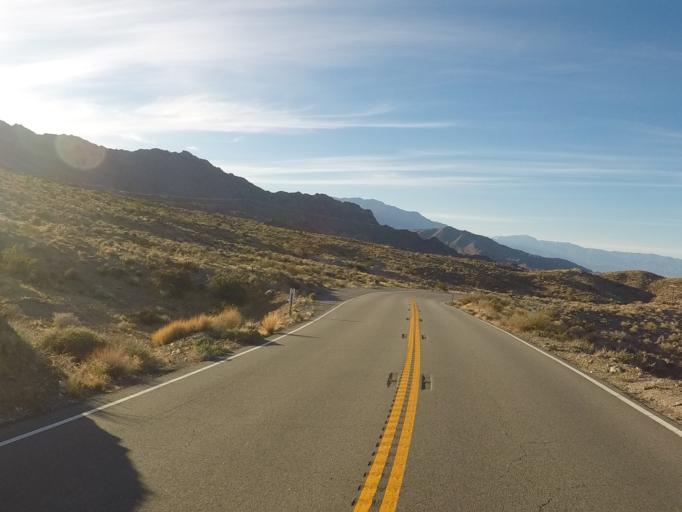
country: US
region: California
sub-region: Riverside County
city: Palm Desert
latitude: 33.6322
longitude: -116.4029
